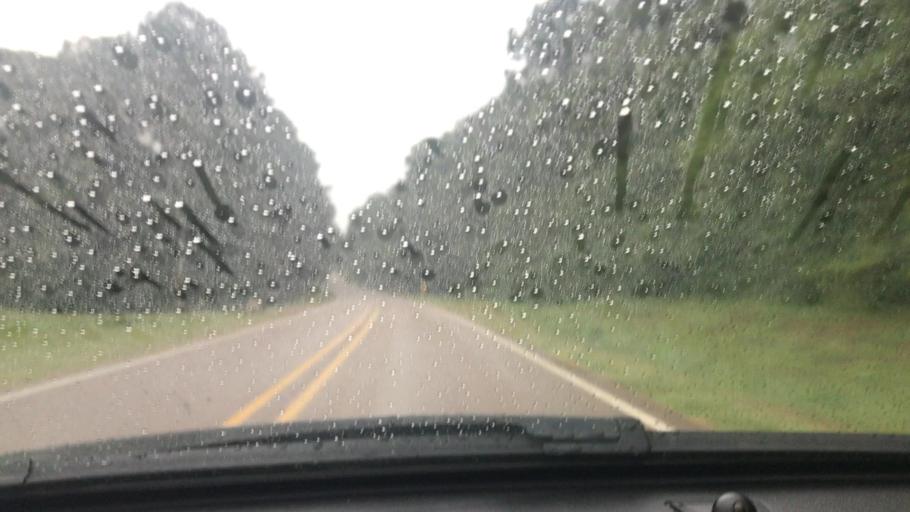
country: US
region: Mississippi
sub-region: Pike County
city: Summit
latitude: 31.2910
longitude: -90.4938
